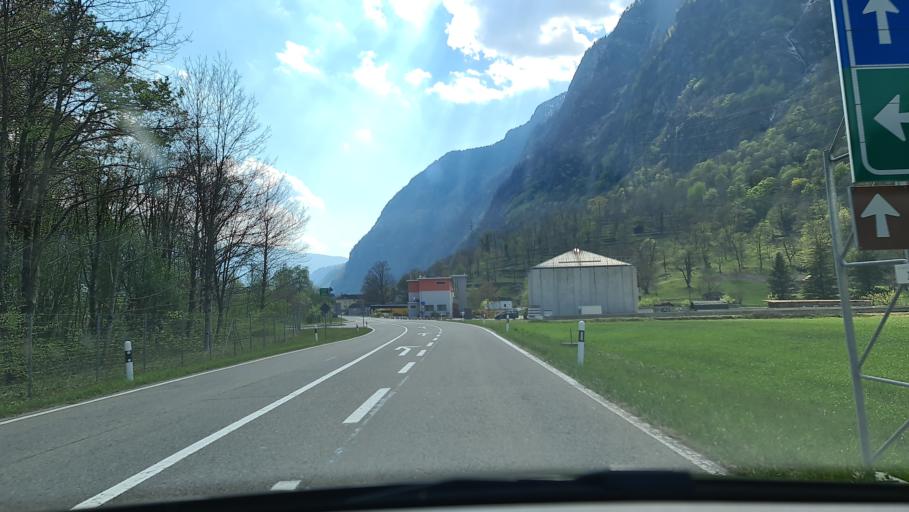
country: CH
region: Grisons
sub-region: Moesa District
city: Santa Maria in Calanca
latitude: 46.3186
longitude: 9.2000
